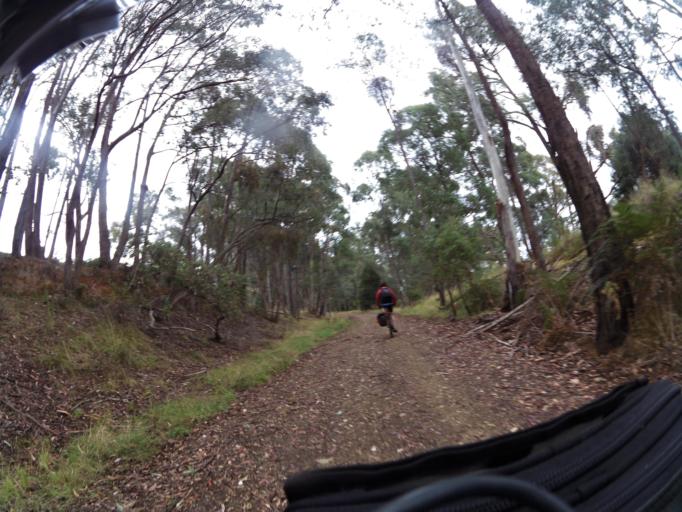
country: AU
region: New South Wales
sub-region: Greater Hume Shire
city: Holbrook
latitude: -36.1513
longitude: 147.4849
